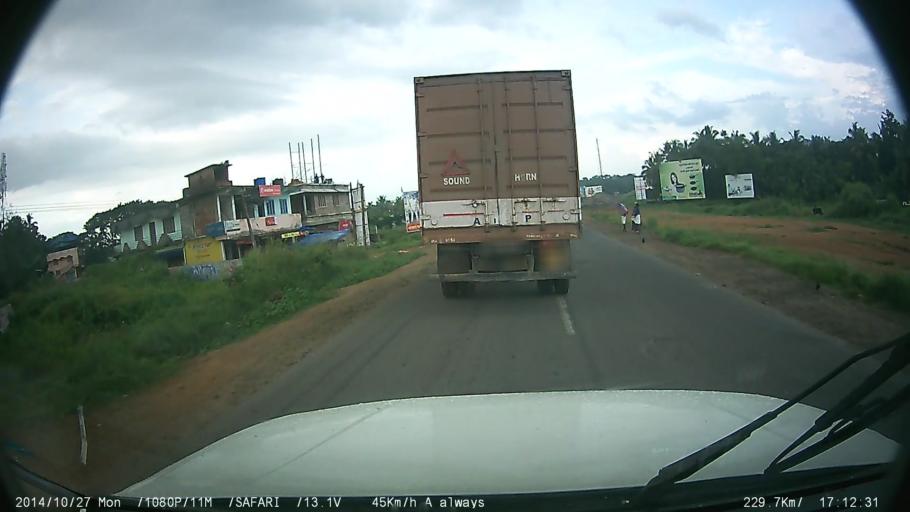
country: IN
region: Kerala
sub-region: Thrissur District
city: Chelakara
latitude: 10.6120
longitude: 76.4979
